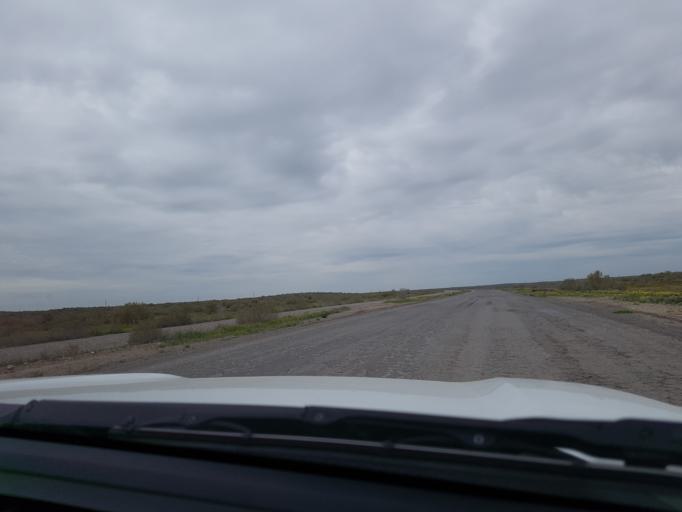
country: TM
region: Mary
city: Bayramaly
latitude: 37.9432
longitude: 62.6352
